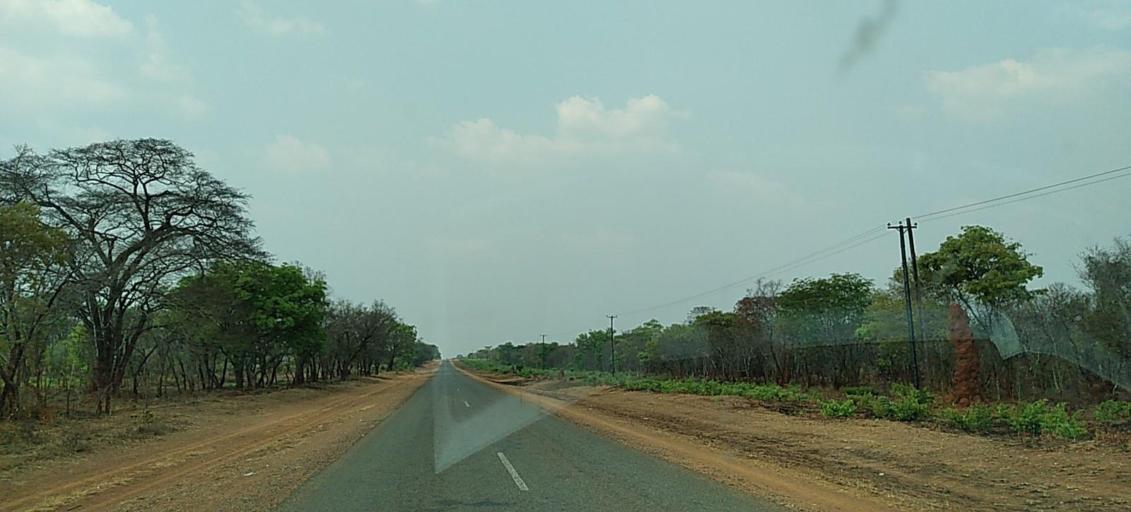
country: ZM
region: North-Western
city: Kabompo
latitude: -13.5769
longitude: 24.2392
